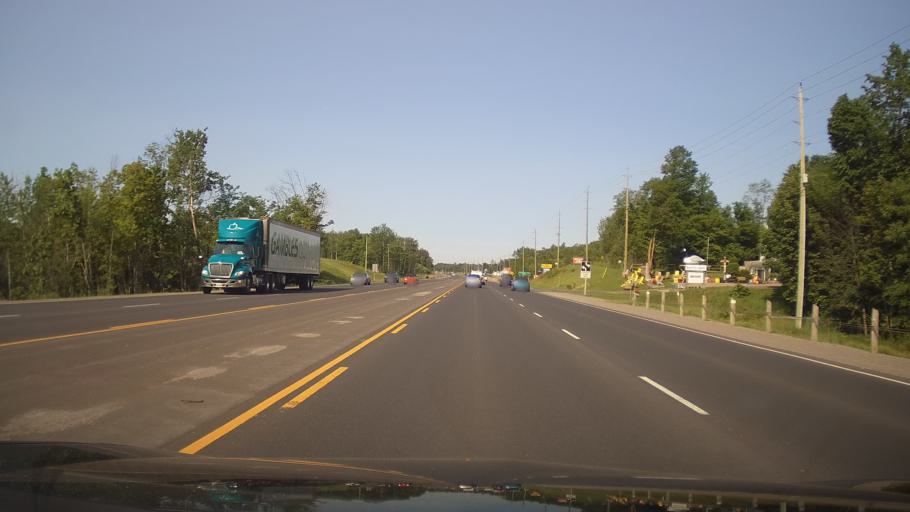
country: CA
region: Ontario
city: Peterborough
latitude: 44.3115
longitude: -78.2234
